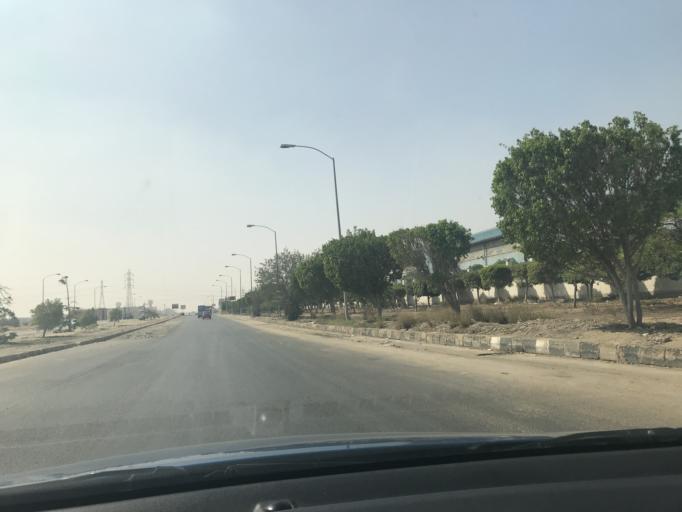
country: EG
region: Eastern Province
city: Bilbays
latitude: 30.2504
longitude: 31.7592
